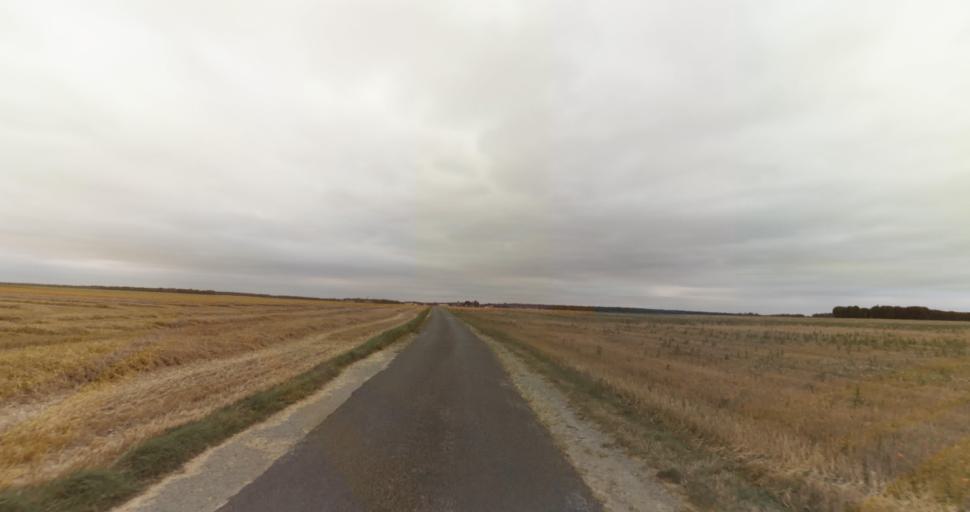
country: FR
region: Haute-Normandie
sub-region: Departement de l'Eure
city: La Couture-Boussey
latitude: 48.9201
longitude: 1.3928
